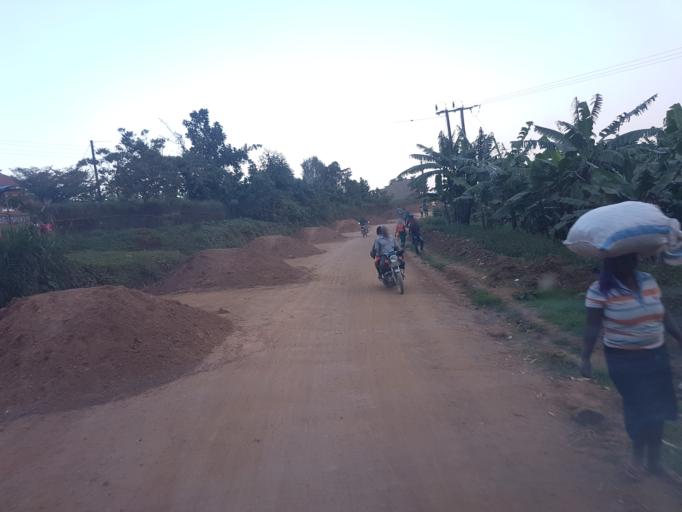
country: UG
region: Western Region
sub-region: Mitoma District
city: Mitoma
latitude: -0.6788
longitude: 29.9420
